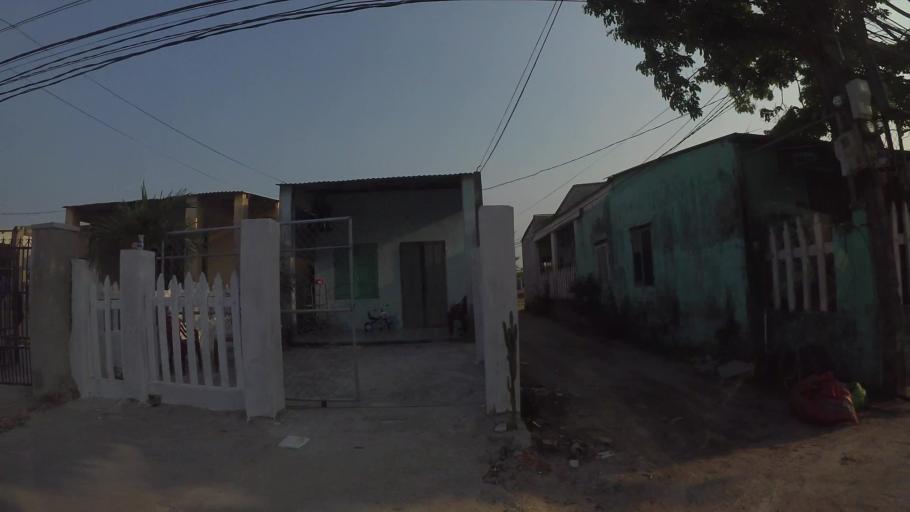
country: VN
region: Da Nang
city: Ngu Hanh Son
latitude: 15.9716
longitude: 108.2503
